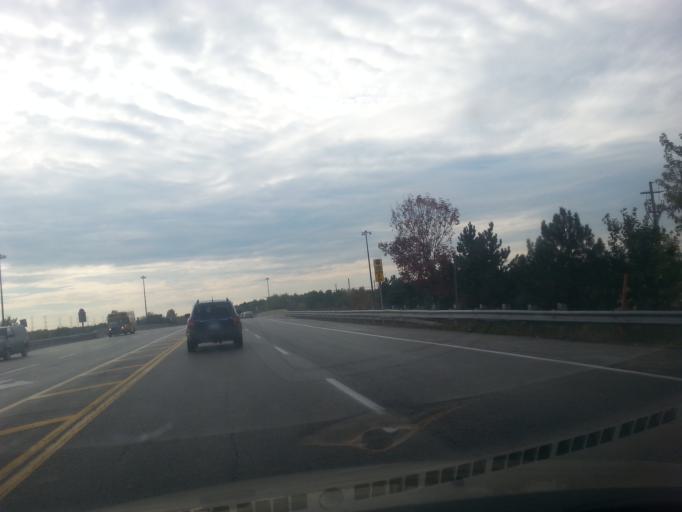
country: CA
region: Ontario
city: Bells Corners
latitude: 45.3136
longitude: -75.8002
